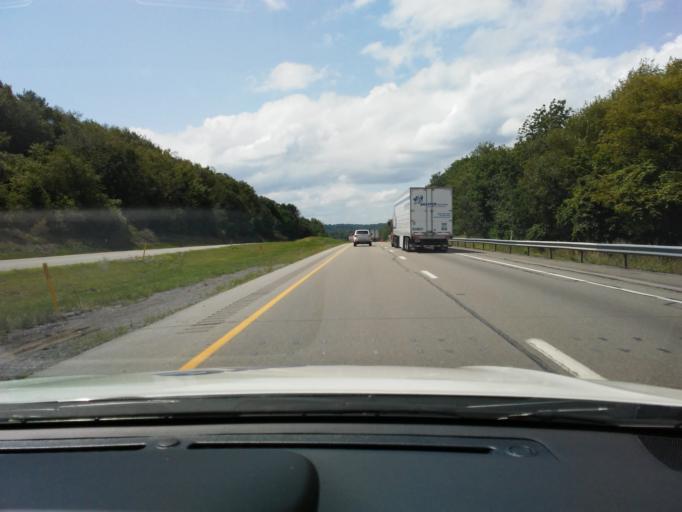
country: US
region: Pennsylvania
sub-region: Jefferson County
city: Brookville
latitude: 41.1850
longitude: -79.1636
